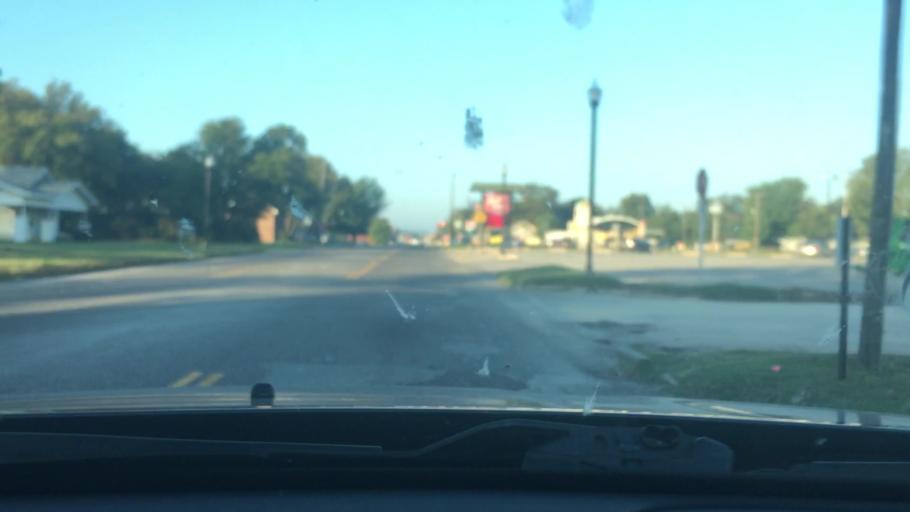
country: US
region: Oklahoma
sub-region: Murray County
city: Davis
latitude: 34.5065
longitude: -97.1136
